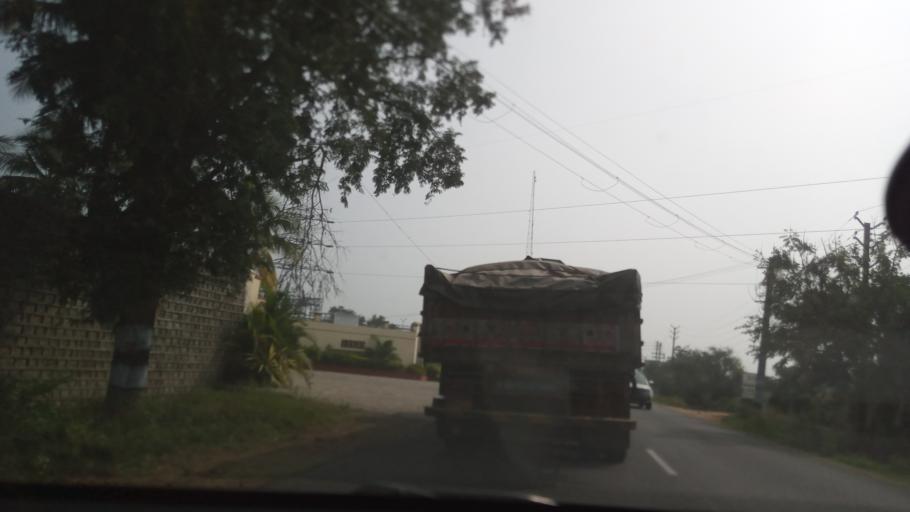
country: IN
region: Tamil Nadu
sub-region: Erode
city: Punjai Puliyampatti
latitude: 11.3996
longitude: 77.1863
